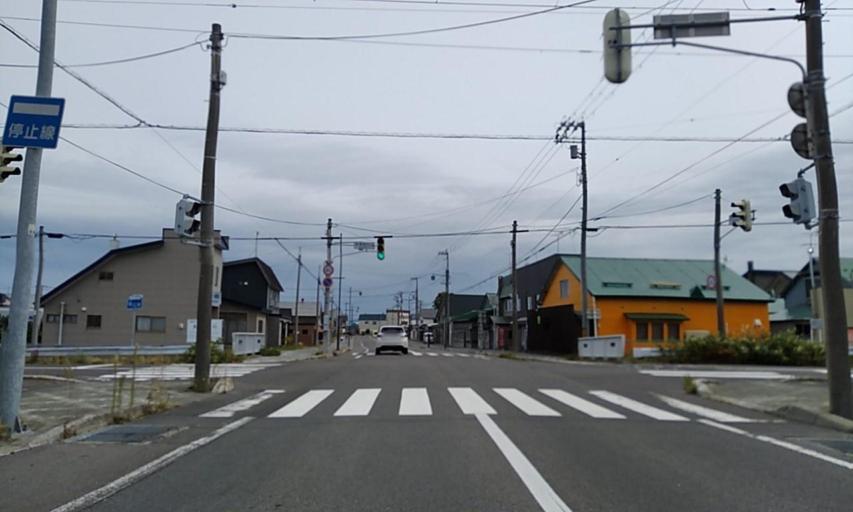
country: JP
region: Hokkaido
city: Rumoi
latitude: 43.8570
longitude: 141.5212
